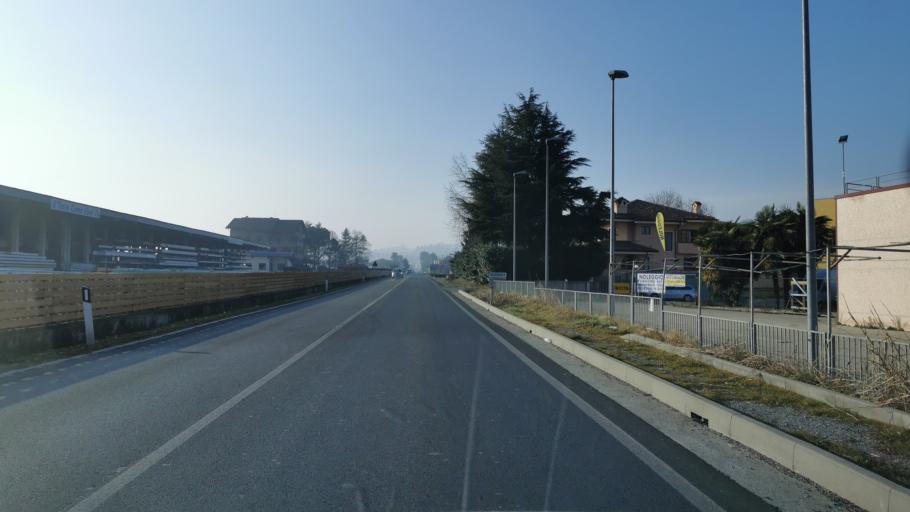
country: IT
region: Piedmont
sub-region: Provincia di Cuneo
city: Pocapaglia
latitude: 44.6961
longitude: 7.8958
